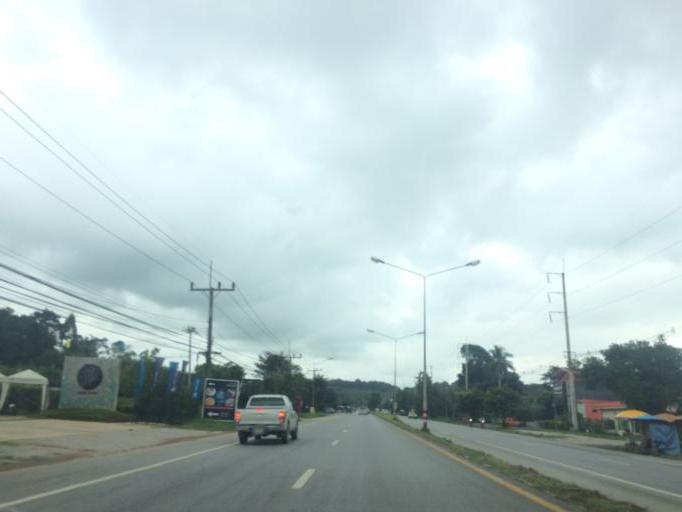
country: TH
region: Chiang Rai
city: Mae Chan
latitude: 20.1072
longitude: 99.8736
